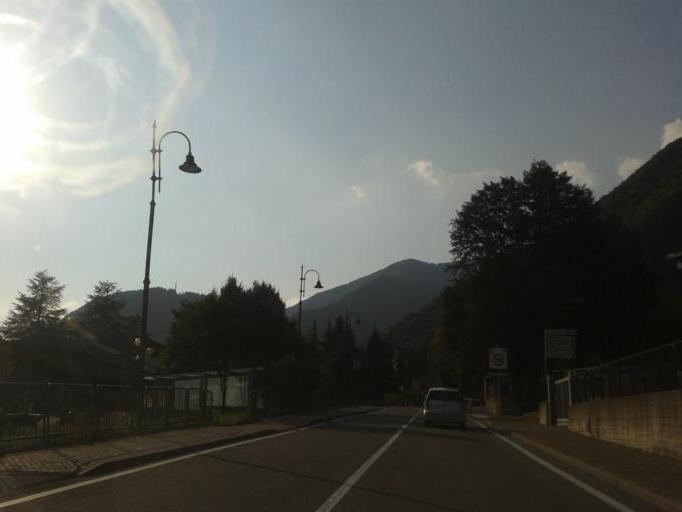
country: IT
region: Trentino-Alto Adige
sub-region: Provincia di Trento
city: Pieve di Ledro
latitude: 45.8947
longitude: 10.7208
